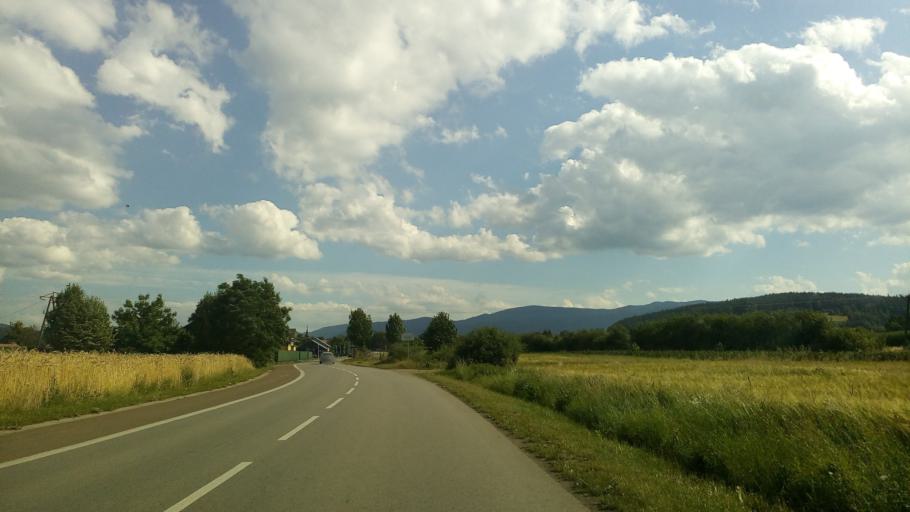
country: PL
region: Lesser Poland Voivodeship
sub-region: Powiat nowosadecki
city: Stary Sacz
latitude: 49.5749
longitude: 20.6362
